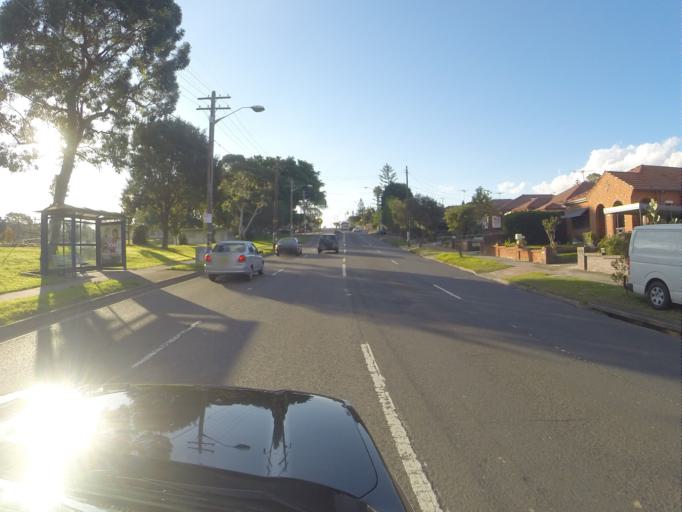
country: AU
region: New South Wales
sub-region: Rockdale
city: Bexley North
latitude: -33.9340
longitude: 151.1102
